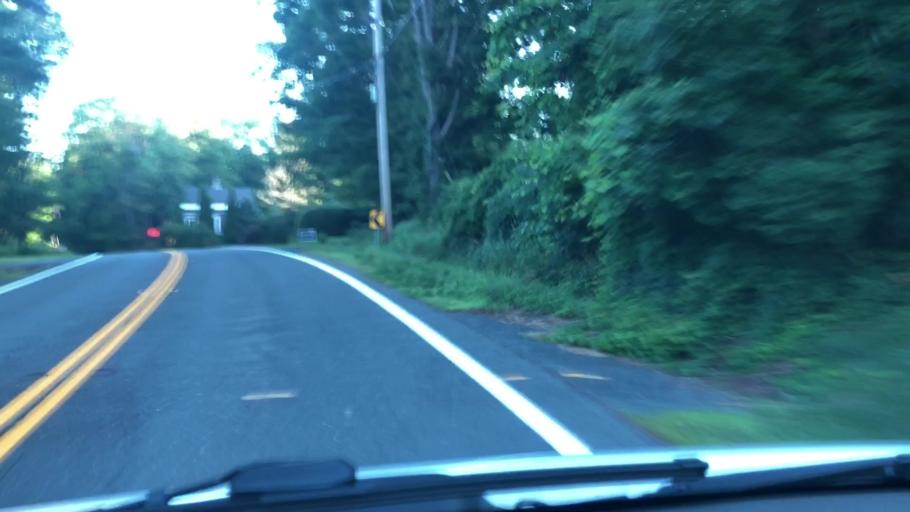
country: US
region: Massachusetts
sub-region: Hampshire County
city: Chesterfield
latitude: 42.3689
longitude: -72.9099
